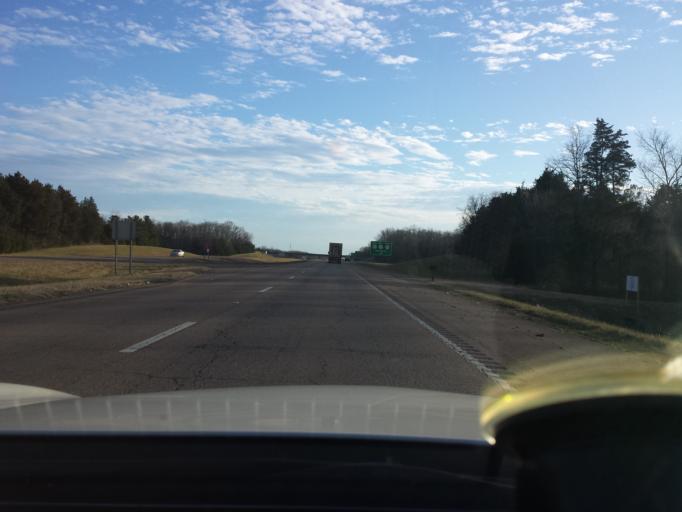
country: US
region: Mississippi
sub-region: Clay County
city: West Point
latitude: 33.4928
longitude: -88.6591
